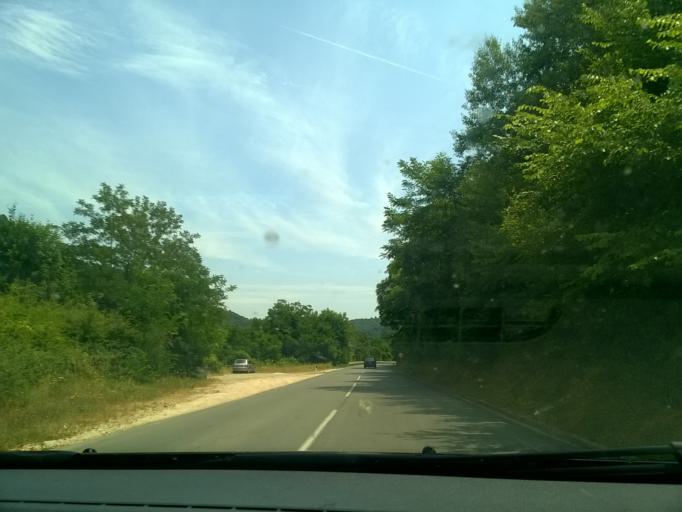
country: RS
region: Central Serbia
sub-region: Nisavski Okrug
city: Aleksinac
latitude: 43.6511
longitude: 21.7278
